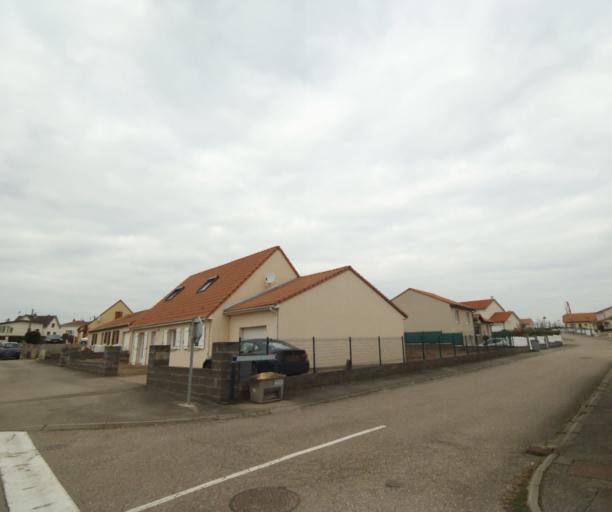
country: FR
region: Lorraine
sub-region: Departement de Meurthe-et-Moselle
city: Mancieulles
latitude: 49.2778
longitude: 5.9021
